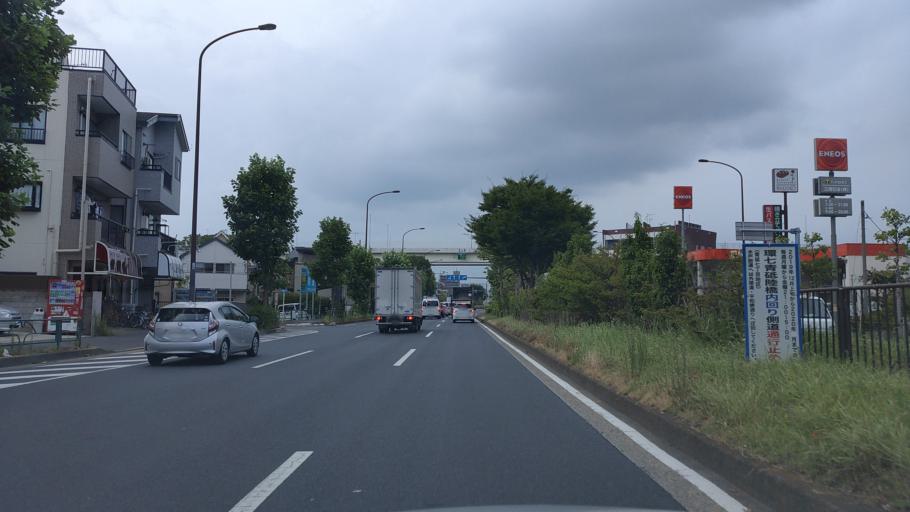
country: JP
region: Tokyo
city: Urayasu
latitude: 35.6956
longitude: 139.8823
